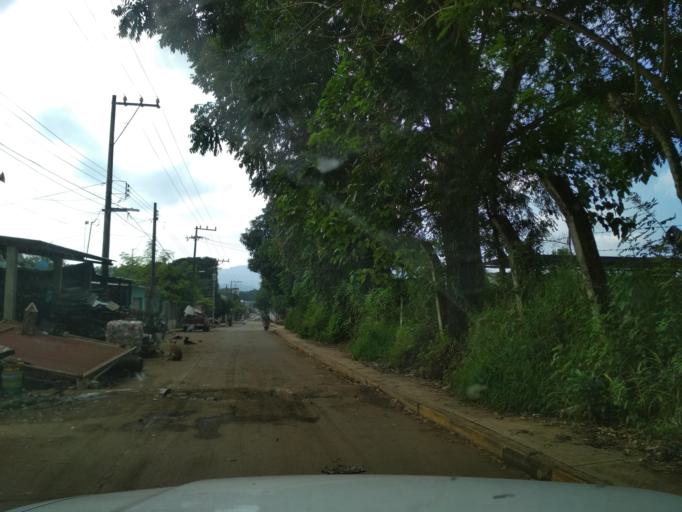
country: MX
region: Veracruz
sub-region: San Andres Tuxtla
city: Matacapan
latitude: 18.4409
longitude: -95.1773
